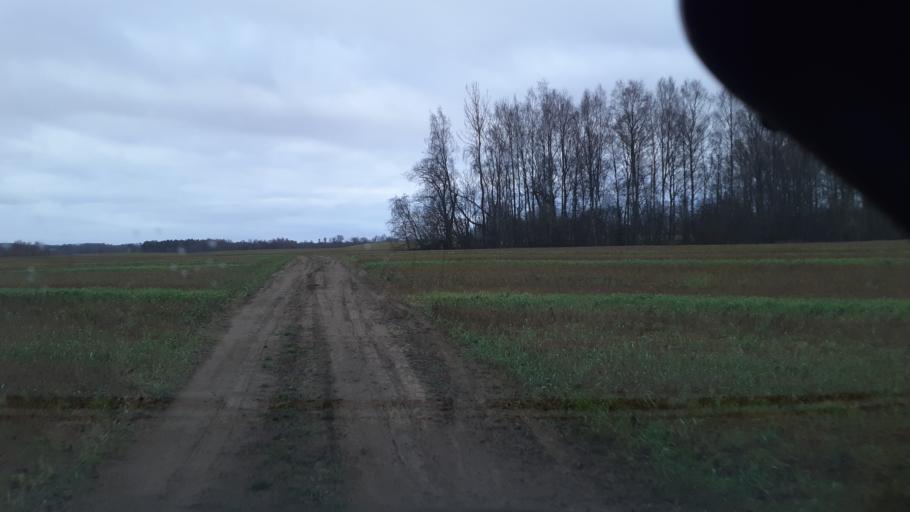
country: LV
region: Kuldigas Rajons
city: Kuldiga
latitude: 56.8846
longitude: 21.7695
